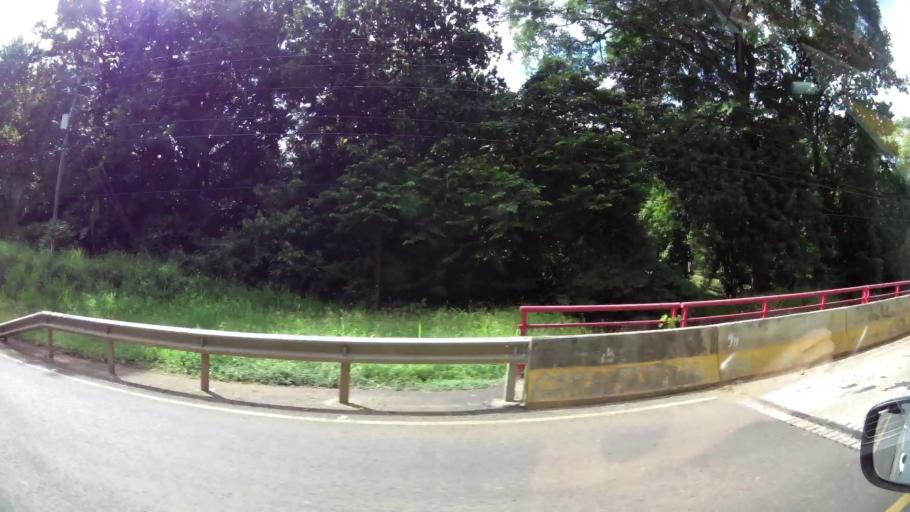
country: CR
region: Guanacaste
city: Hojancha
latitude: 10.1174
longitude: -85.3439
